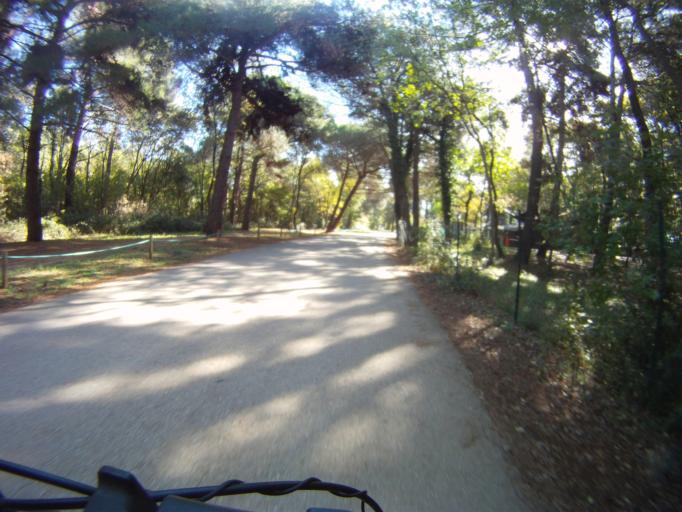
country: HR
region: Istarska
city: Novigrad
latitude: 45.3291
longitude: 13.5445
